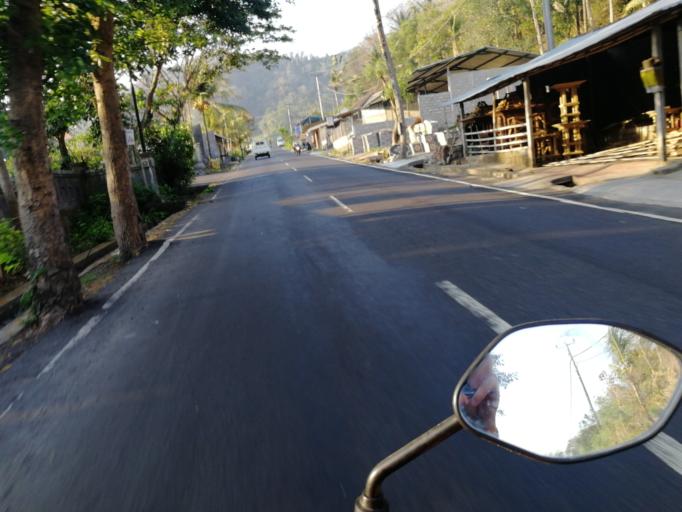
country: ID
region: Bali
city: Banjar Kangkaang
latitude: -8.3612
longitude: 115.6119
